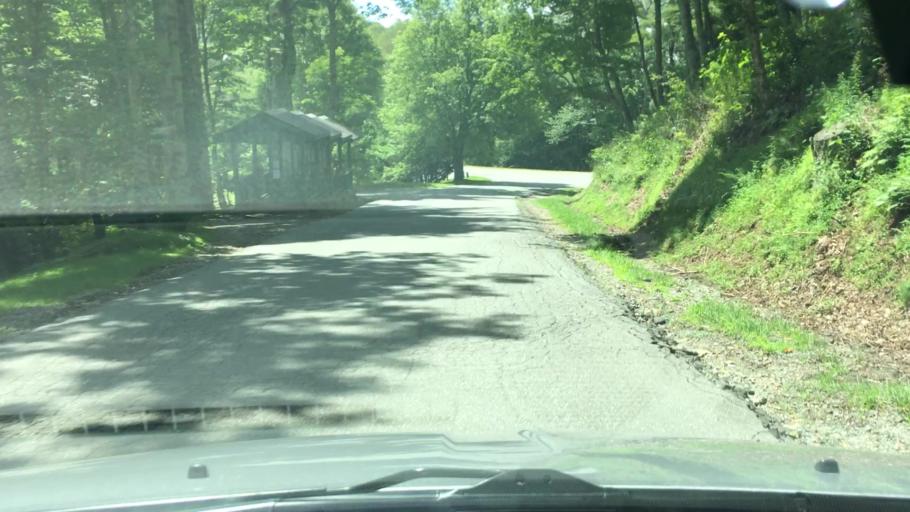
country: US
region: North Carolina
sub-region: Madison County
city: Mars Hill
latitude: 35.9705
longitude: -82.5022
